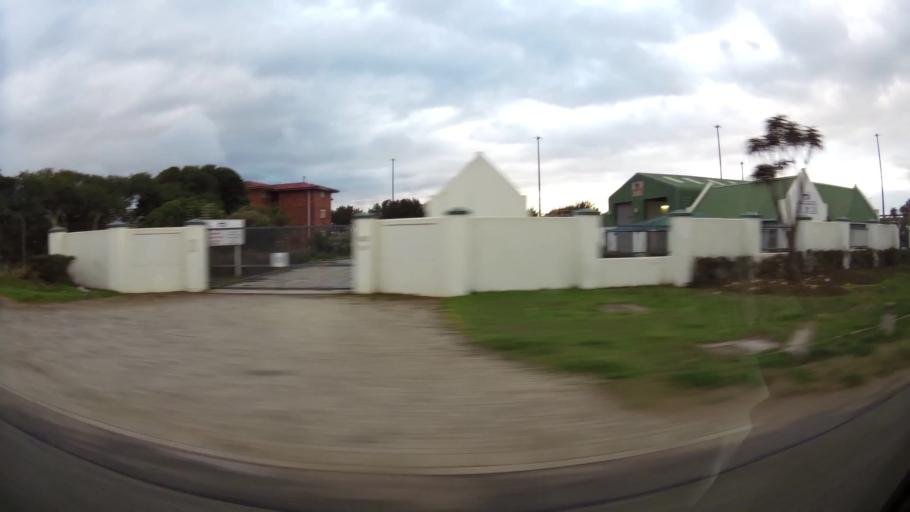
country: ZA
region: Eastern Cape
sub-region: Nelson Mandela Bay Metropolitan Municipality
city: Port Elizabeth
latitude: -33.9300
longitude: 25.6085
